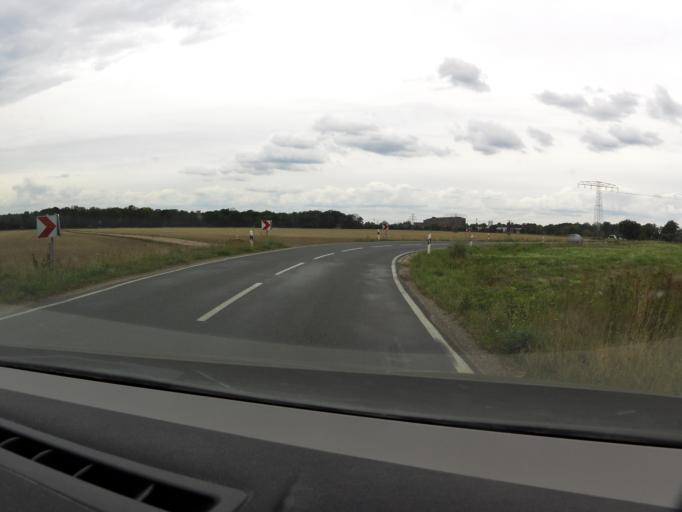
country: DE
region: Saxony-Anhalt
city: Vockerode
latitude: 51.8369
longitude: 12.3764
